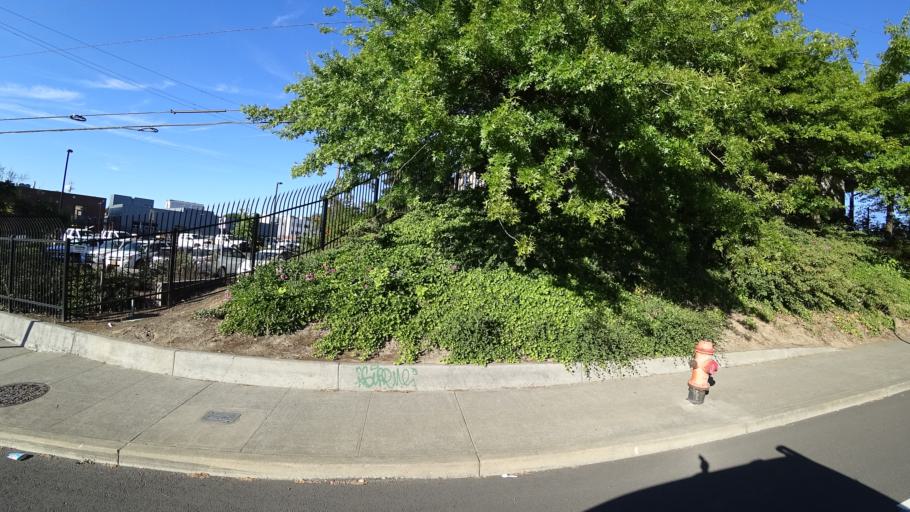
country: US
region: Oregon
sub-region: Multnomah County
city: Portland
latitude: 45.5363
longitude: -122.6742
